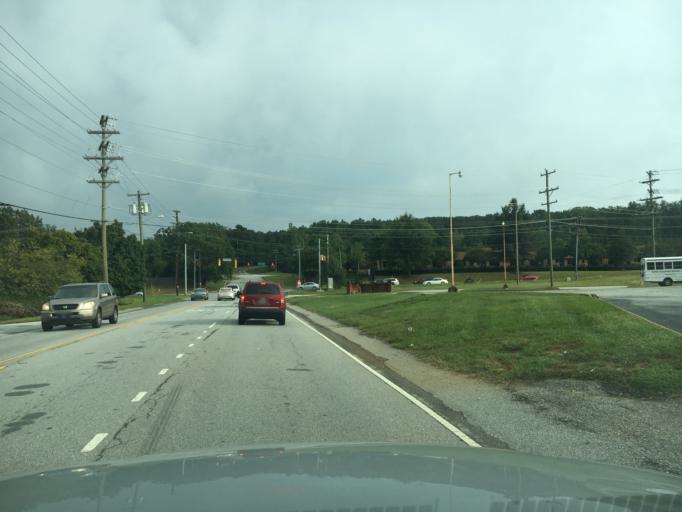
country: US
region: South Carolina
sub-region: Greenville County
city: Wade Hampton
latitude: 34.8457
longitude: -82.3105
